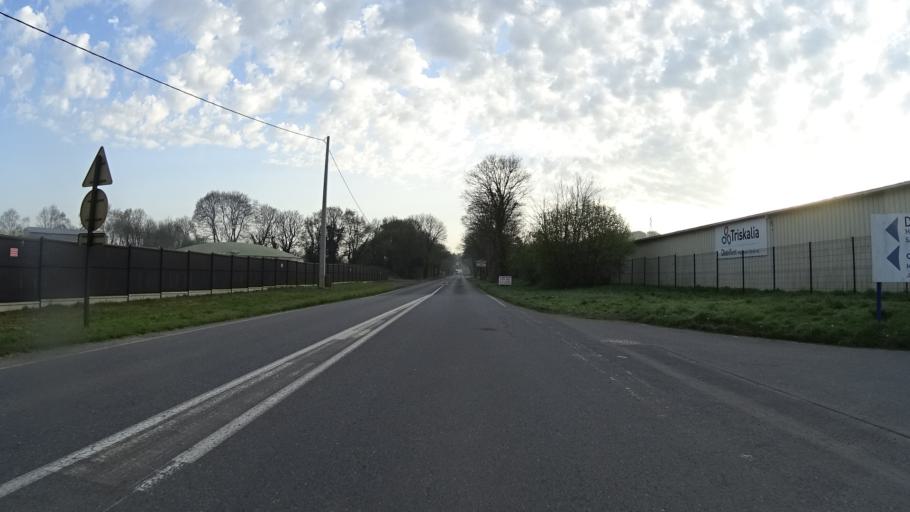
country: FR
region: Brittany
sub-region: Departement du Finistere
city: Landerneau
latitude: 48.4550
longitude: -4.2379
